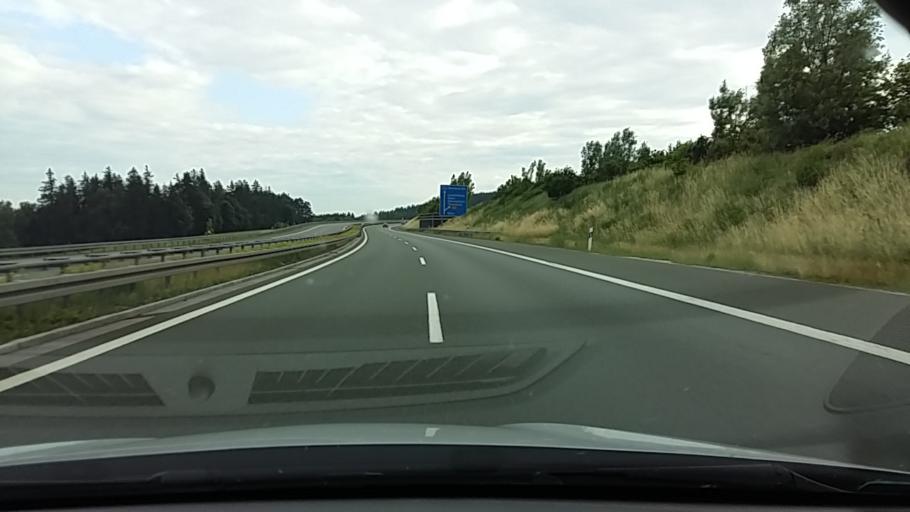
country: DE
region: Bavaria
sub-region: Upper Palatinate
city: Leuchtenberg
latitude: 49.5826
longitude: 12.2779
